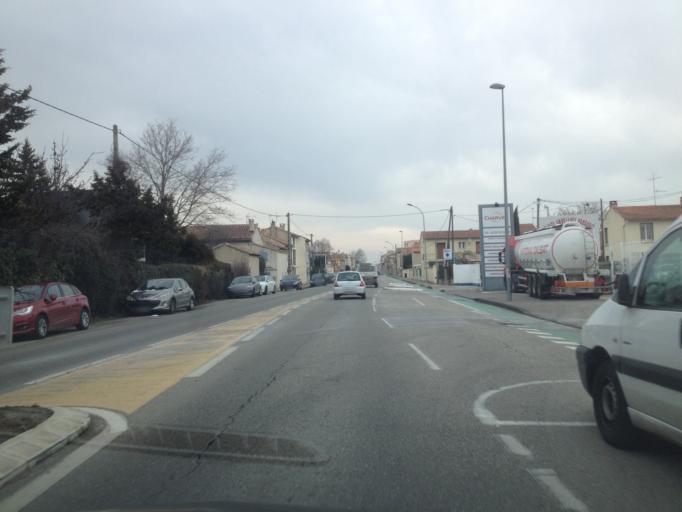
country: FR
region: Provence-Alpes-Cote d'Azur
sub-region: Departement du Vaucluse
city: Sorgues
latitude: 44.0012
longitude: 4.8685
